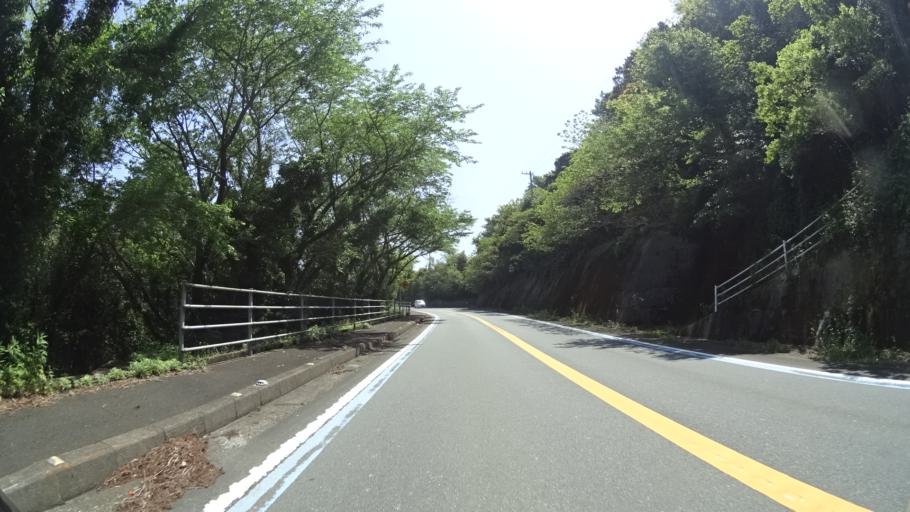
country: JP
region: Ehime
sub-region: Nishiuwa-gun
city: Ikata-cho
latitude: 33.4466
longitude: 132.2646
